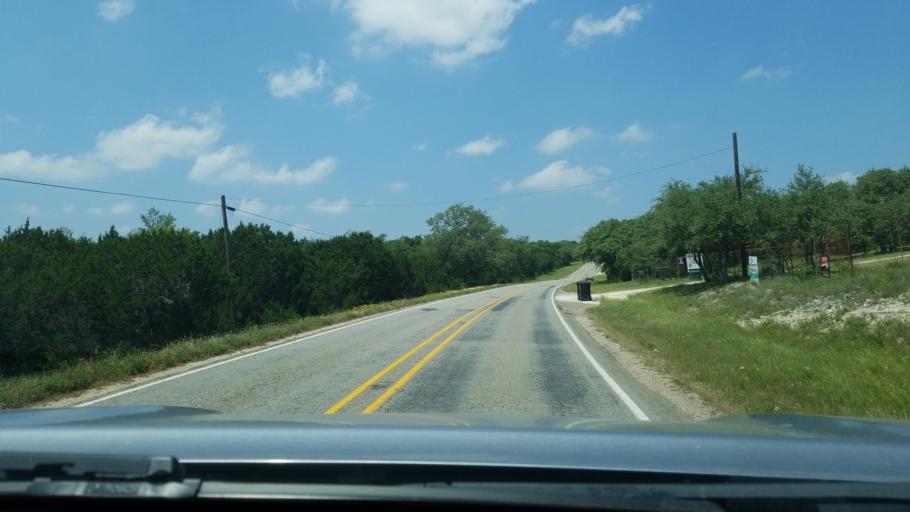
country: US
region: Texas
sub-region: Hays County
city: Woodcreek
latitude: 30.0695
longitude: -98.2194
